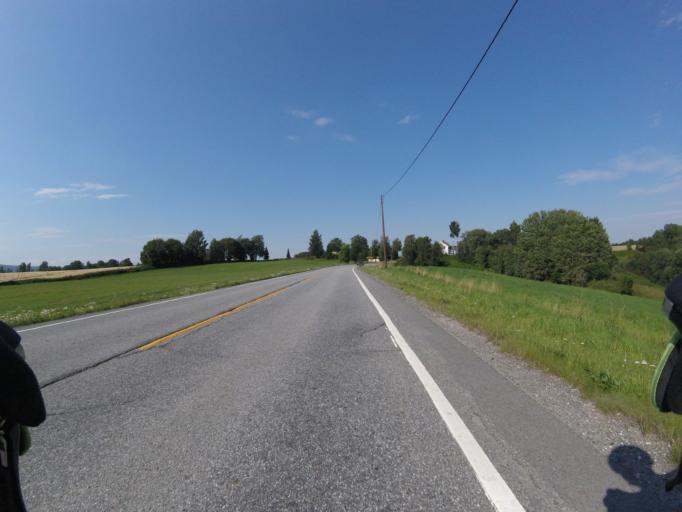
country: NO
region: Akershus
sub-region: Ullensaker
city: Klofta
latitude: 60.0528
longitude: 11.1180
